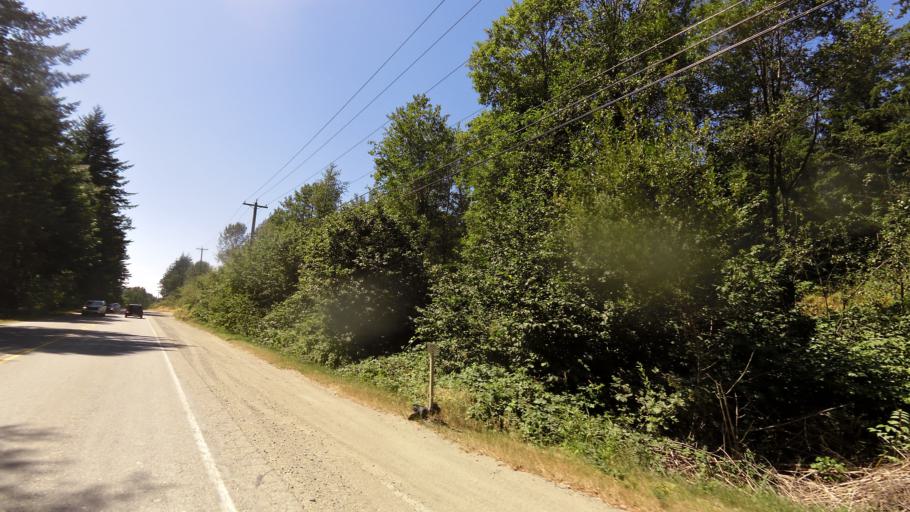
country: CA
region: British Columbia
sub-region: Fraser Valley Regional District
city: Chilliwack
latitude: 49.2013
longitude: -122.0416
